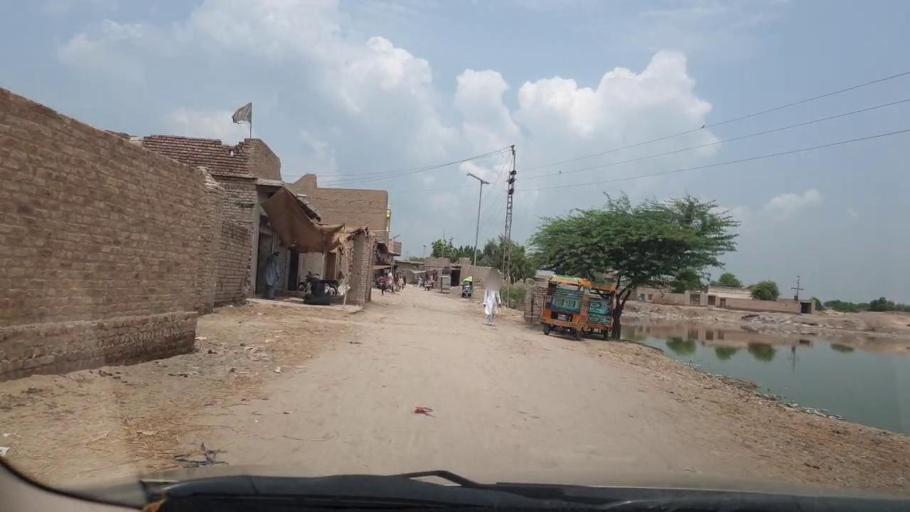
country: PK
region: Sindh
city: Larkana
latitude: 27.5597
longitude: 68.1235
